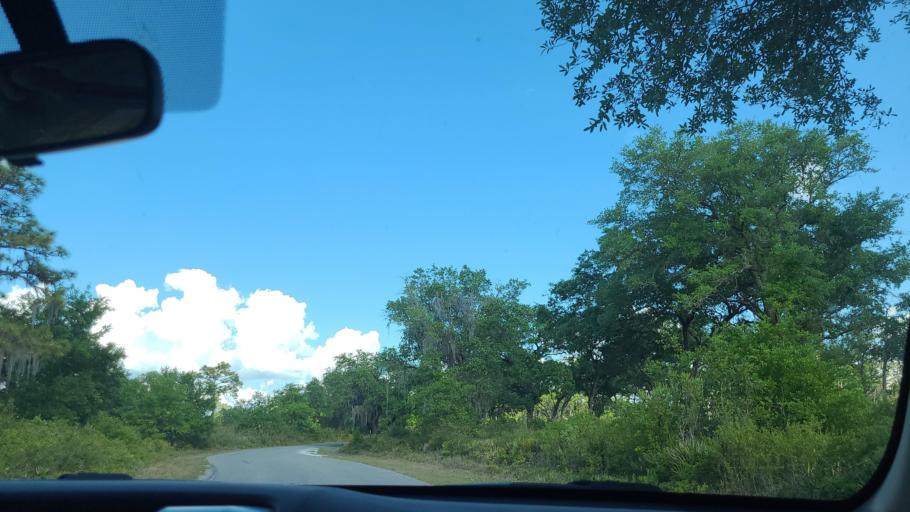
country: US
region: Florida
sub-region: Polk County
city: Babson Park
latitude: 27.9588
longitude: -81.3778
